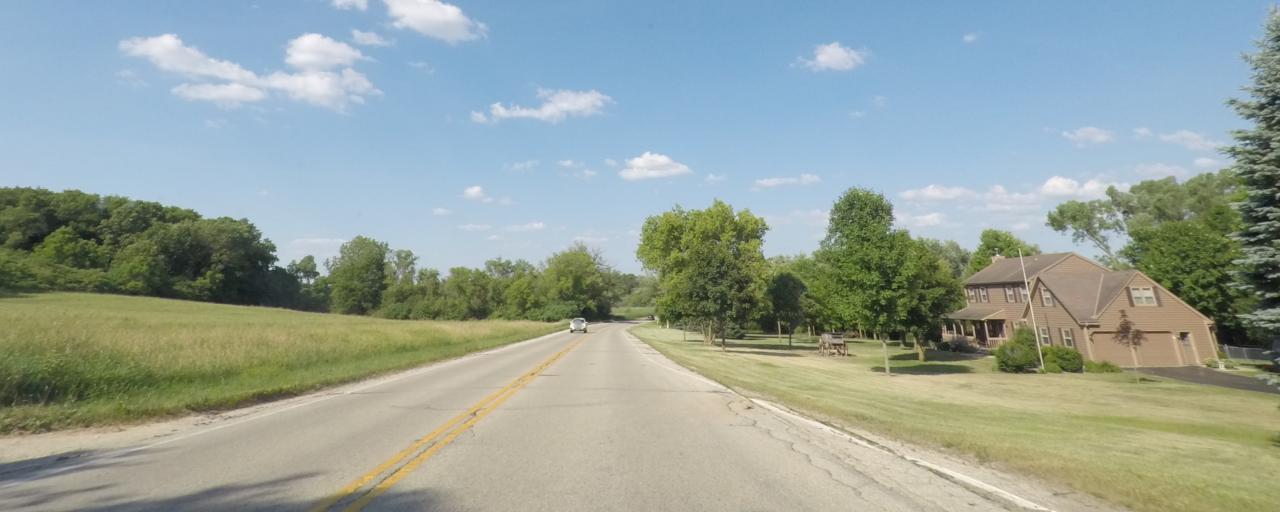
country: US
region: Wisconsin
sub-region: Waukesha County
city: Big Bend
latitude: 42.8497
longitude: -88.2563
